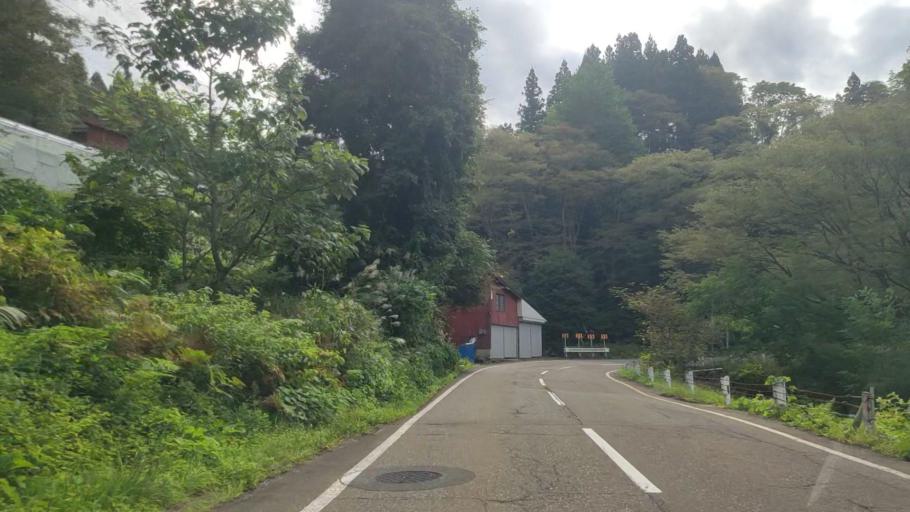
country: JP
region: Niigata
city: Arai
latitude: 36.9312
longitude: 138.2984
